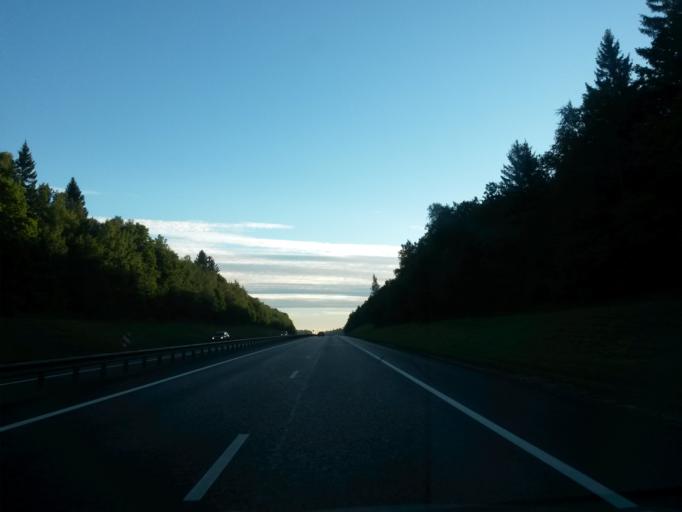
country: RU
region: Moskovskaya
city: Svatkovo
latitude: 56.3679
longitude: 38.3026
